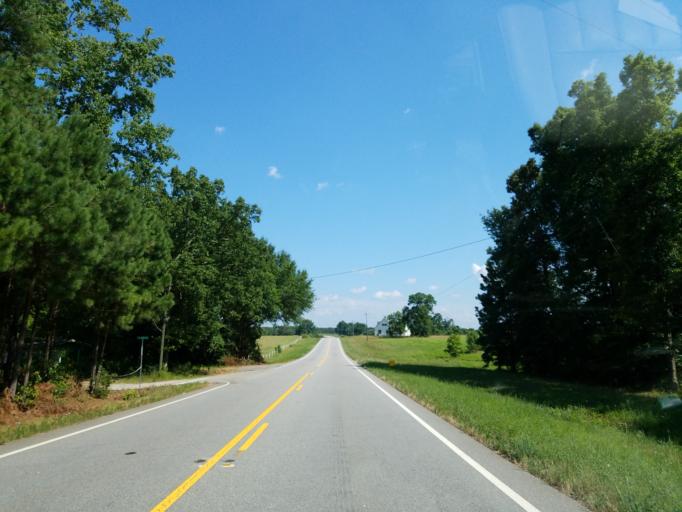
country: US
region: Georgia
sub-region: Lamar County
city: Barnesville
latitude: 32.9404
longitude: -84.0890
